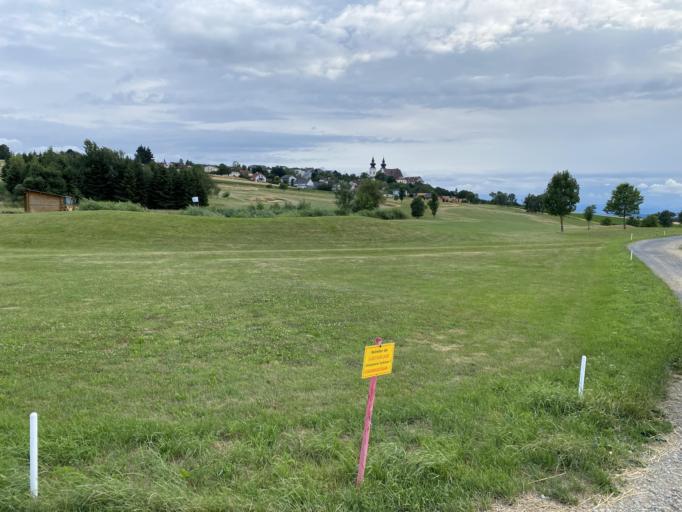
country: AT
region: Lower Austria
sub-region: Politischer Bezirk Melk
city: Marbach an der Donau
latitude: 48.2321
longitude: 15.1607
